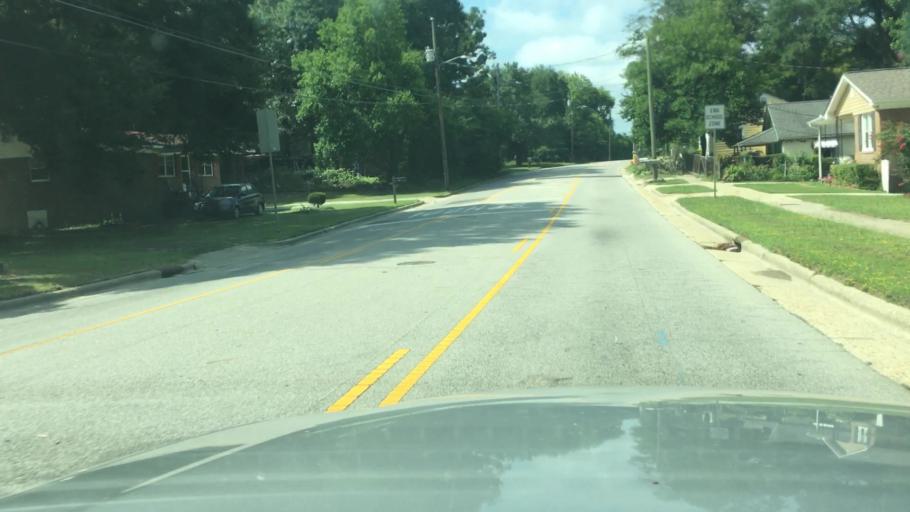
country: US
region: North Carolina
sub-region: Cumberland County
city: Fayetteville
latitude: 35.0276
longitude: -78.8980
